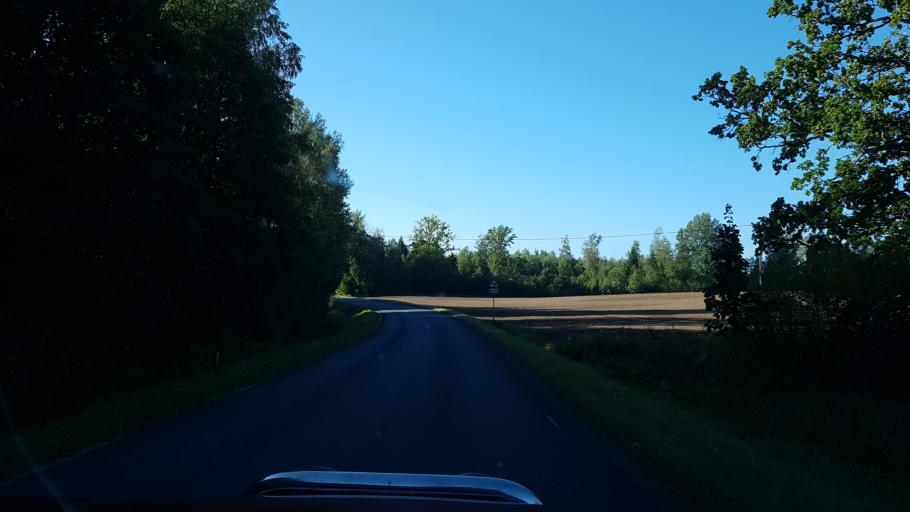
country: EE
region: Jogevamaa
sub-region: Jogeva linn
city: Jogeva
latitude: 58.7272
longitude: 26.5168
